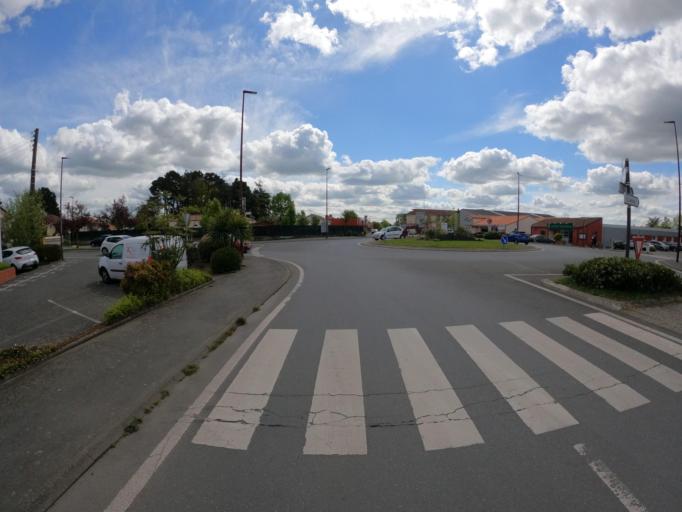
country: FR
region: Pays de la Loire
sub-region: Departement de la Loire-Atlantique
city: Clisson
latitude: 47.0960
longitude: -1.2816
